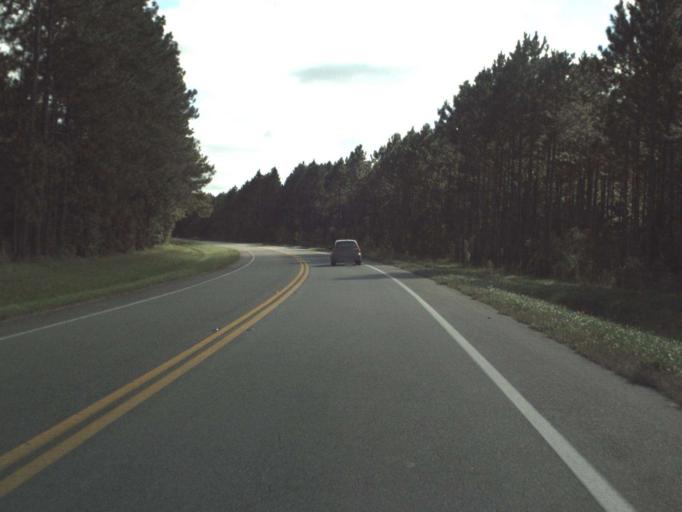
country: US
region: Florida
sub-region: Calhoun County
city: Blountstown
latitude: 30.4029
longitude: -85.0872
